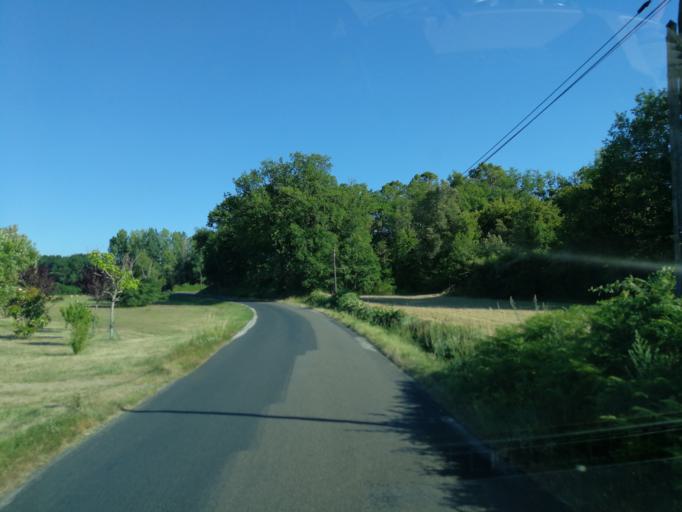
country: FR
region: Midi-Pyrenees
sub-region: Departement du Lot
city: Gourdon
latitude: 44.7676
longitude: 1.3694
